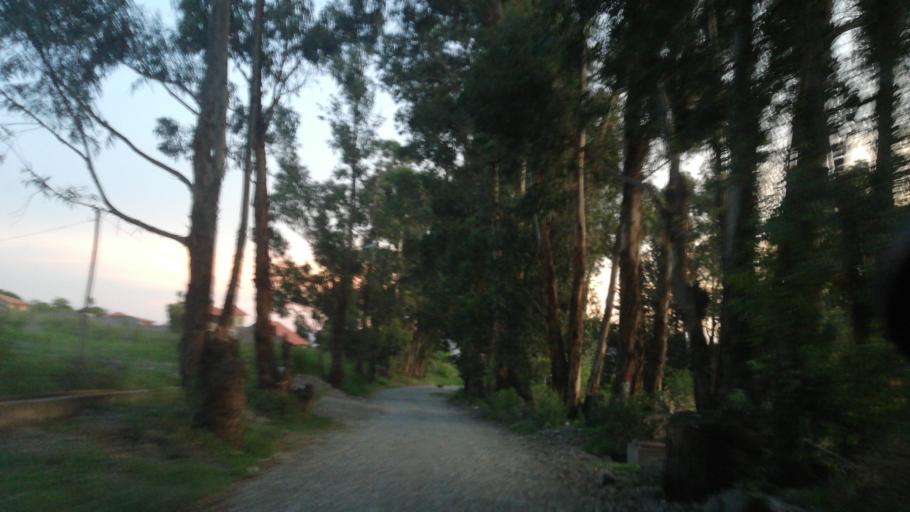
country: BO
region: Cochabamba
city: Cochabamba
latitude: -17.3228
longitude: -66.2087
